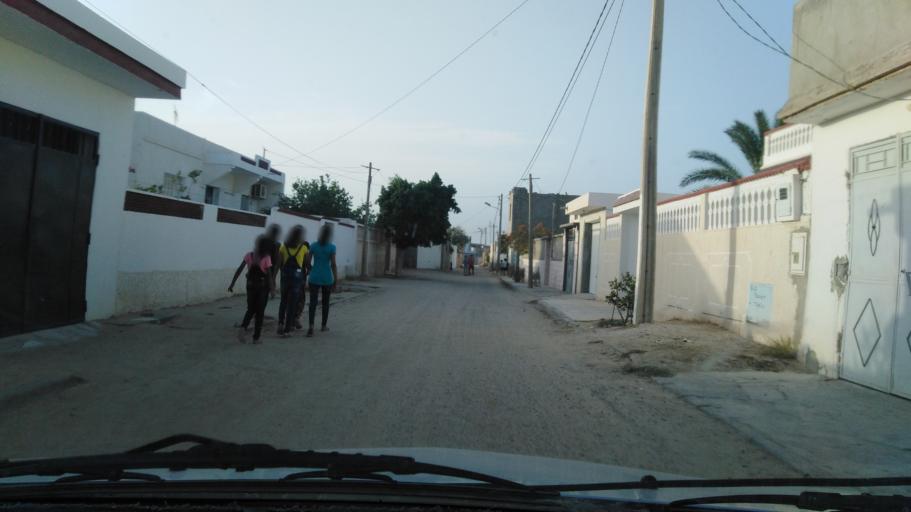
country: TN
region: Qabis
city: Gabes
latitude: 33.9542
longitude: 9.9962
